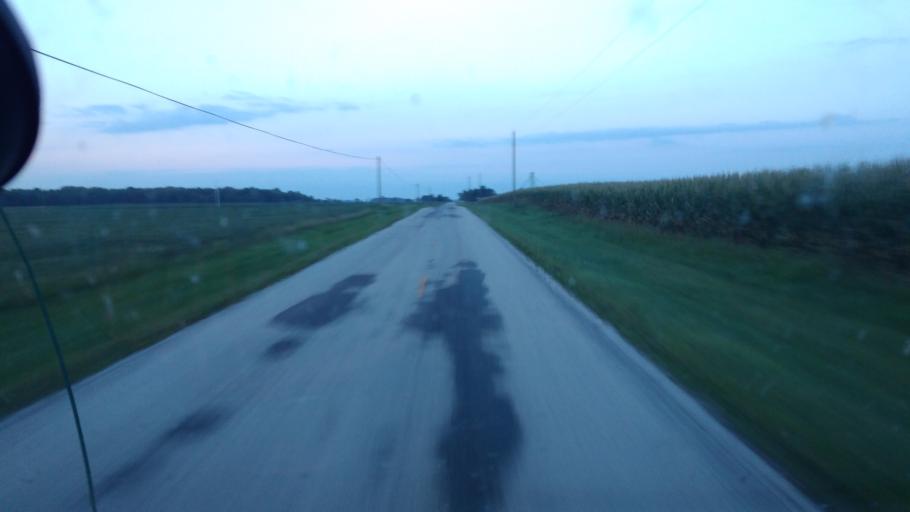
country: US
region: Ohio
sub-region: Hardin County
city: Kenton
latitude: 40.6722
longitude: -83.4988
